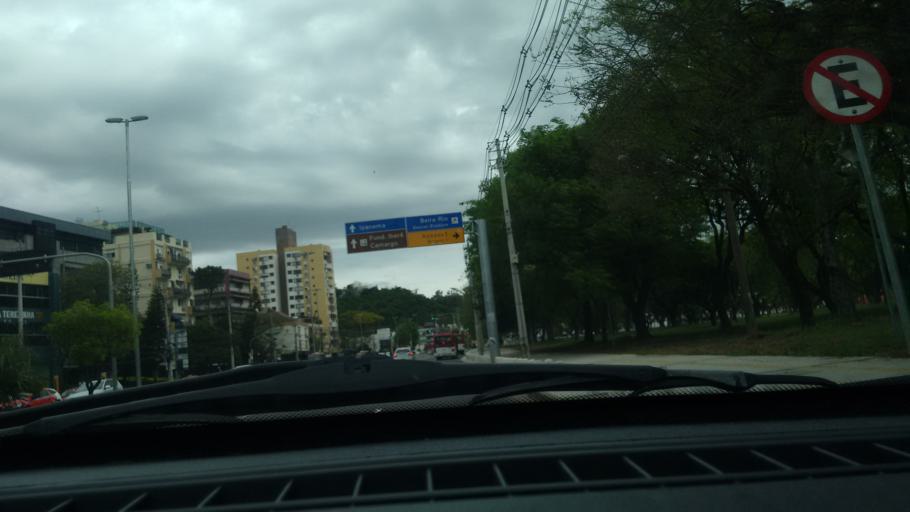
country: BR
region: Rio Grande do Sul
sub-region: Porto Alegre
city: Porto Alegre
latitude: -30.0615
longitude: -51.2312
